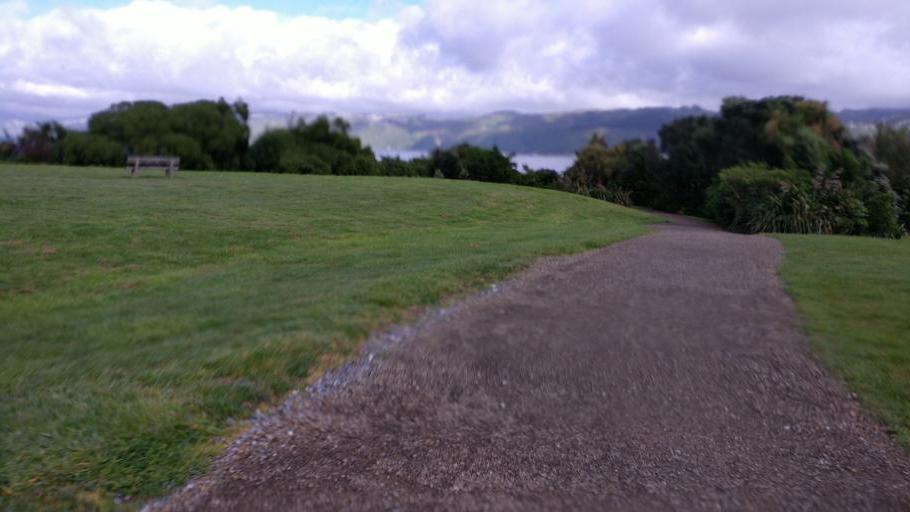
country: NZ
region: Wellington
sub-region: Lower Hutt City
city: Lower Hutt
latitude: -41.2369
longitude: 174.8973
